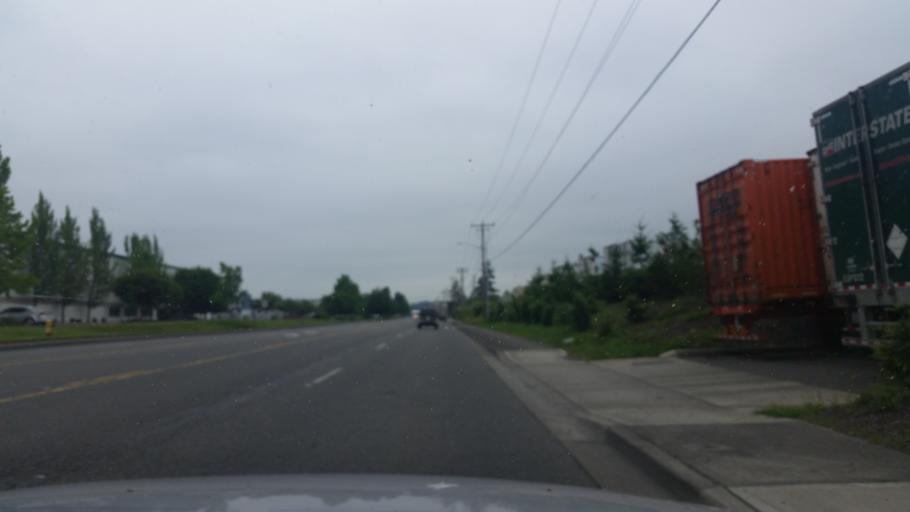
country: US
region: Washington
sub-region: Pierce County
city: Sumner
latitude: 47.2250
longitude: -122.2400
